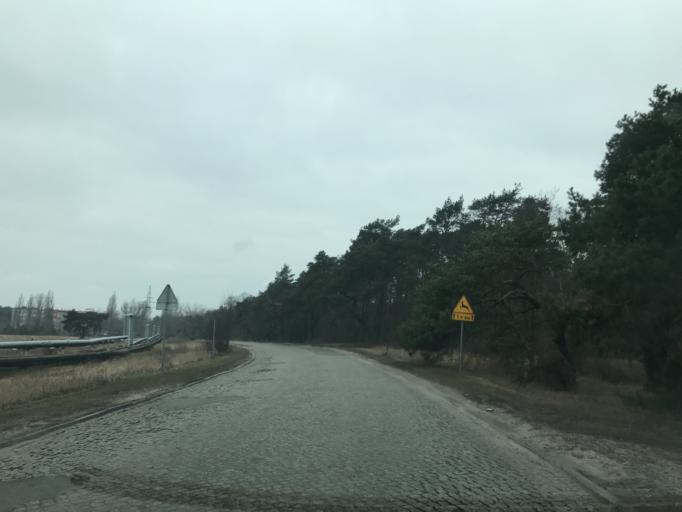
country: PL
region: Kujawsko-Pomorskie
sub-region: Powiat bydgoski
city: Osielsko
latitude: 53.1058
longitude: 18.0951
